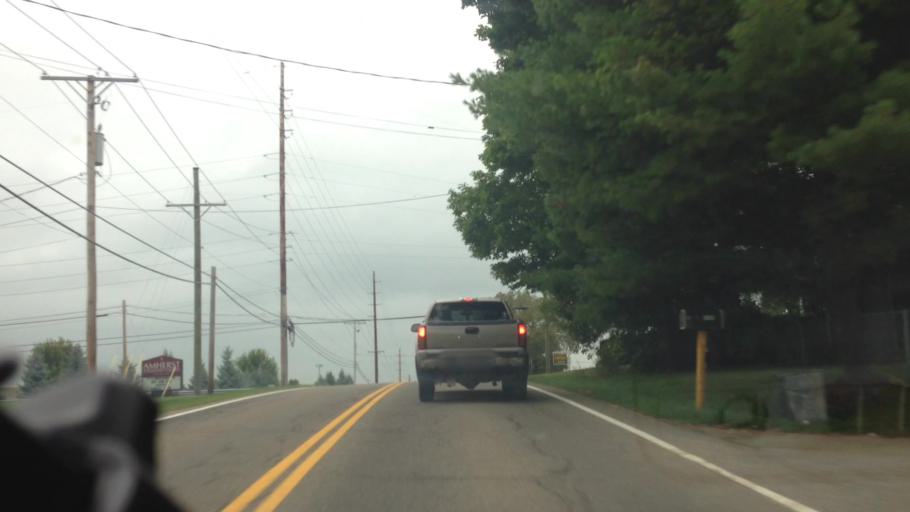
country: US
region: Ohio
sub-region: Stark County
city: Massillon
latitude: 40.8501
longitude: -81.5111
